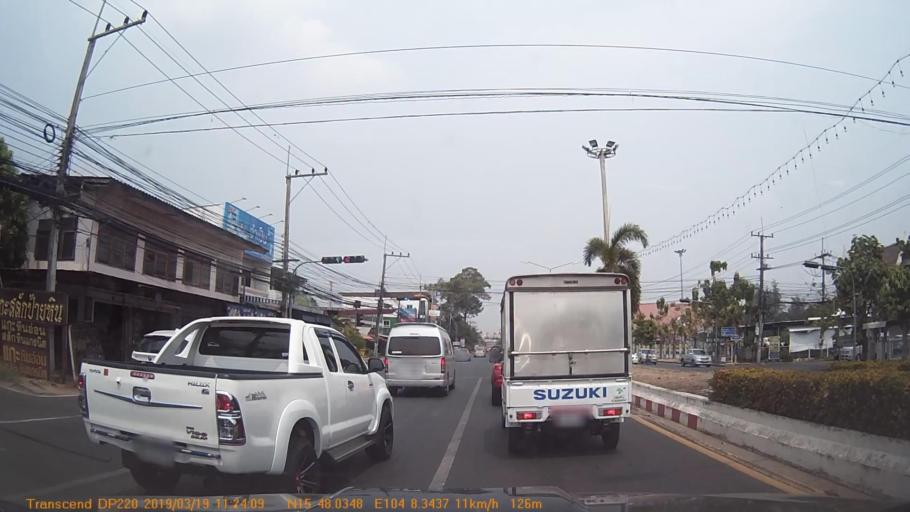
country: TH
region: Yasothon
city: Yasothon
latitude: 15.8006
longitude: 104.1391
